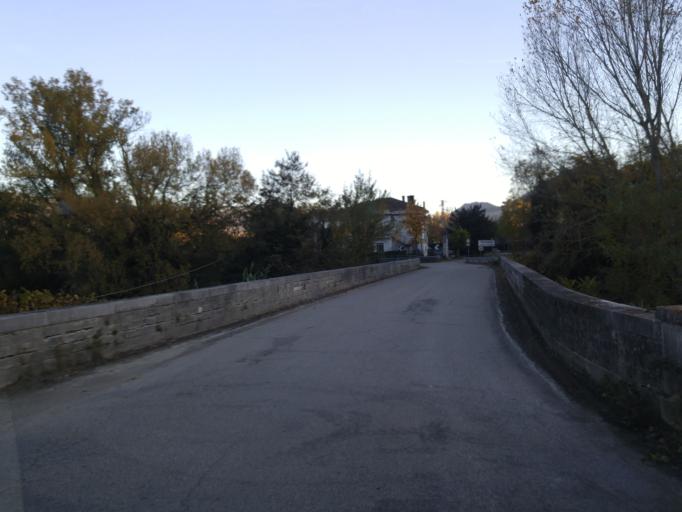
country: IT
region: The Marches
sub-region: Provincia di Pesaro e Urbino
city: Canavaccio
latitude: 43.6759
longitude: 12.7509
